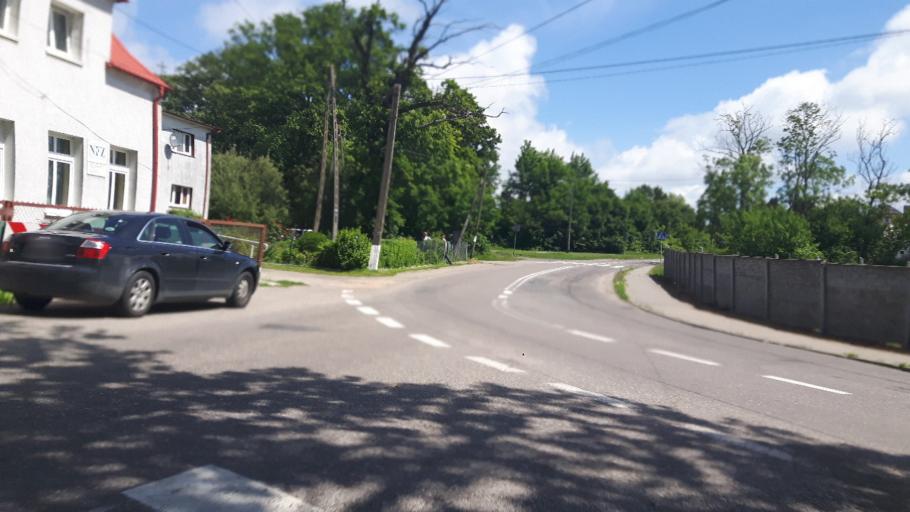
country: PL
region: Pomeranian Voivodeship
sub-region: Powiat slupski
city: Ustka
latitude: 54.5210
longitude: 16.7652
